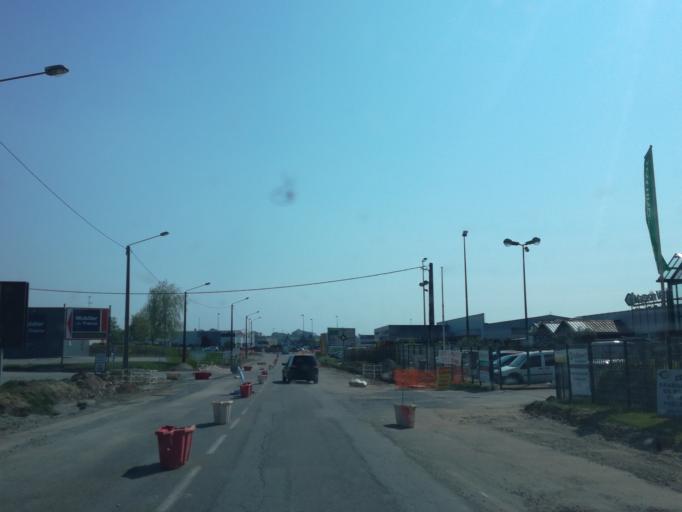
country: FR
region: Brittany
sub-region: Departement du Morbihan
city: Le Sourn
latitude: 48.0428
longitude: -2.9605
